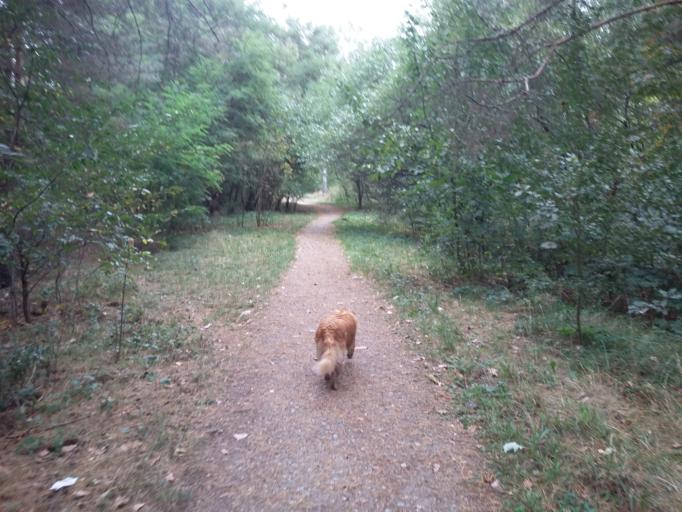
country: PL
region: Lodz Voivodeship
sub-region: Powiat pabianicki
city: Ksawerow
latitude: 51.7220
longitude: 19.3845
